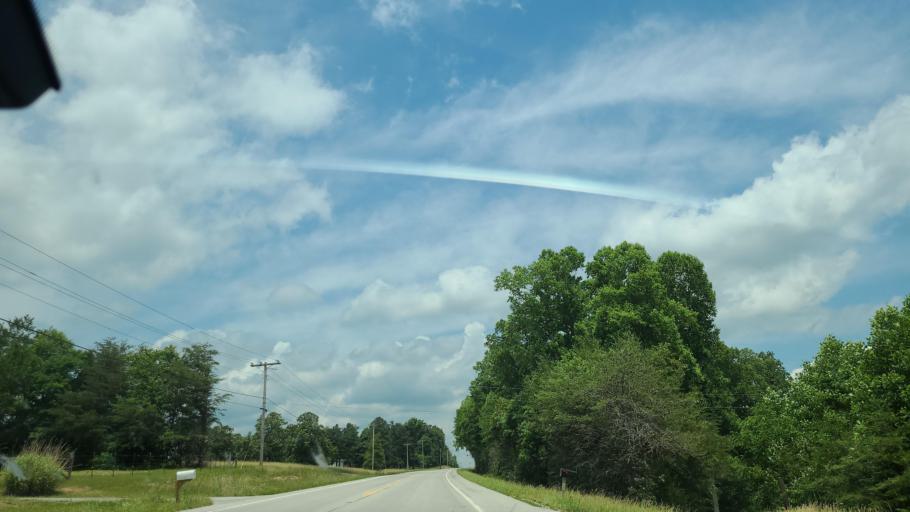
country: US
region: Tennessee
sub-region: Cumberland County
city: Lake Tansi
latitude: 35.8260
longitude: -85.0192
